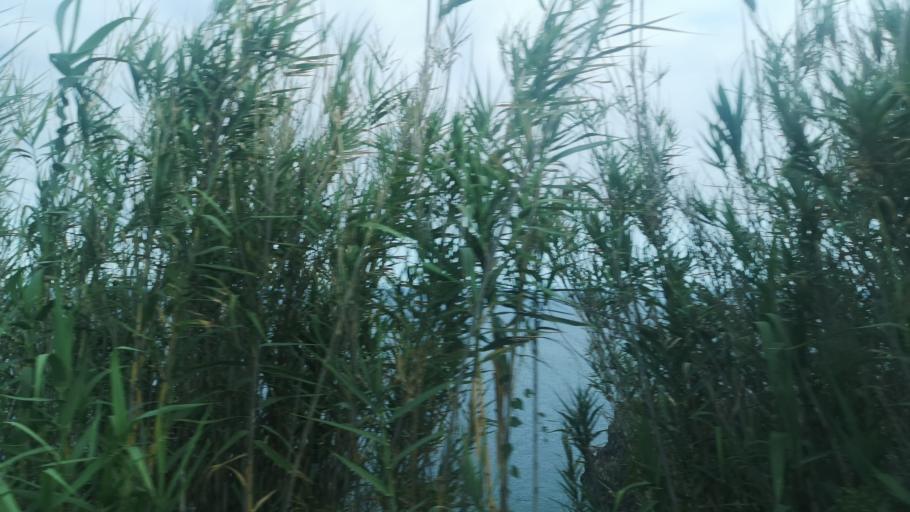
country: PT
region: Madeira
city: Canico
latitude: 32.6510
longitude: -16.8230
